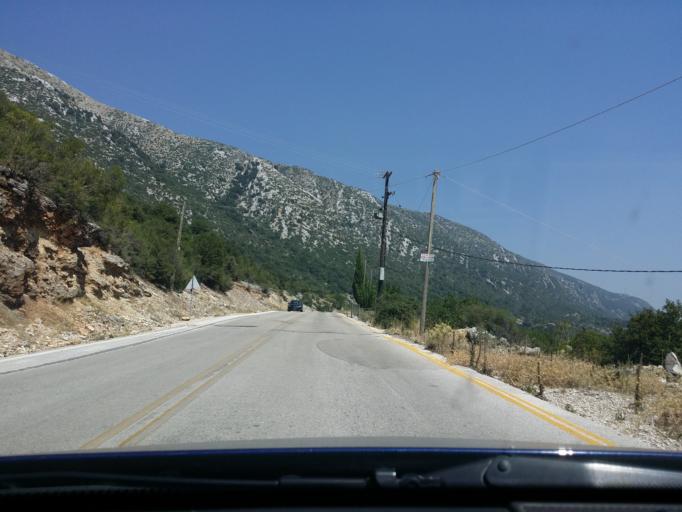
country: GR
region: Epirus
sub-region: Nomos Artas
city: Grammenitsa
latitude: 39.2879
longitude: 20.9760
